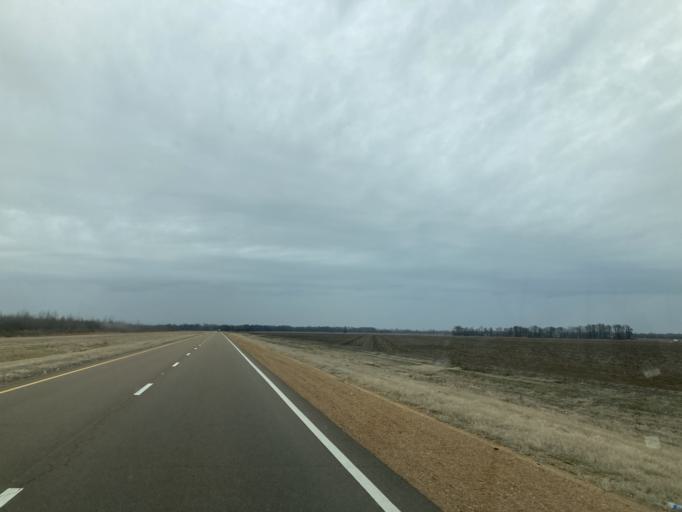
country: US
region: Mississippi
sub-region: Humphreys County
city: Belzoni
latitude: 33.0596
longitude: -90.4704
